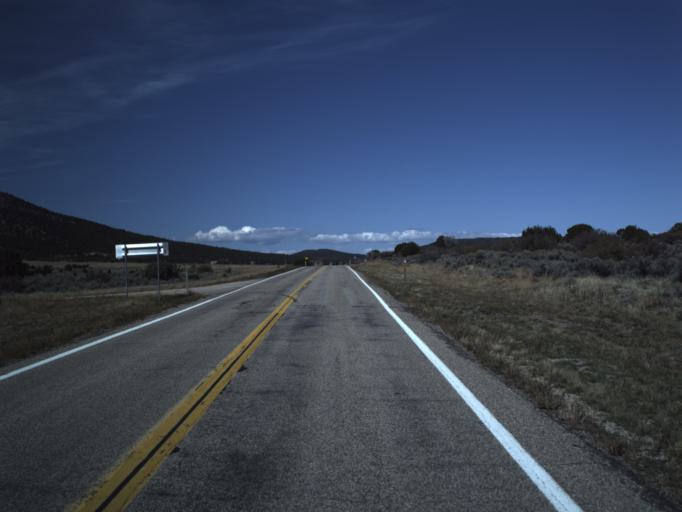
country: US
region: Utah
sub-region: Washington County
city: Enterprise
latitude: 37.4892
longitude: -113.6299
